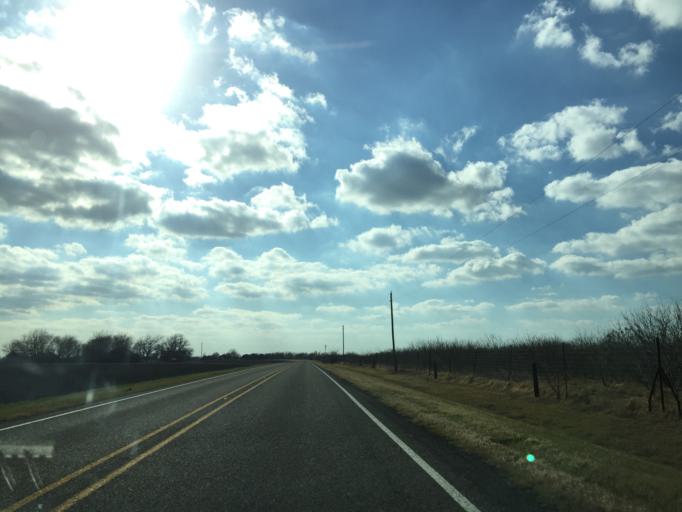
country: US
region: Texas
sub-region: Williamson County
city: Taylor
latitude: 30.6505
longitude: -97.3951
